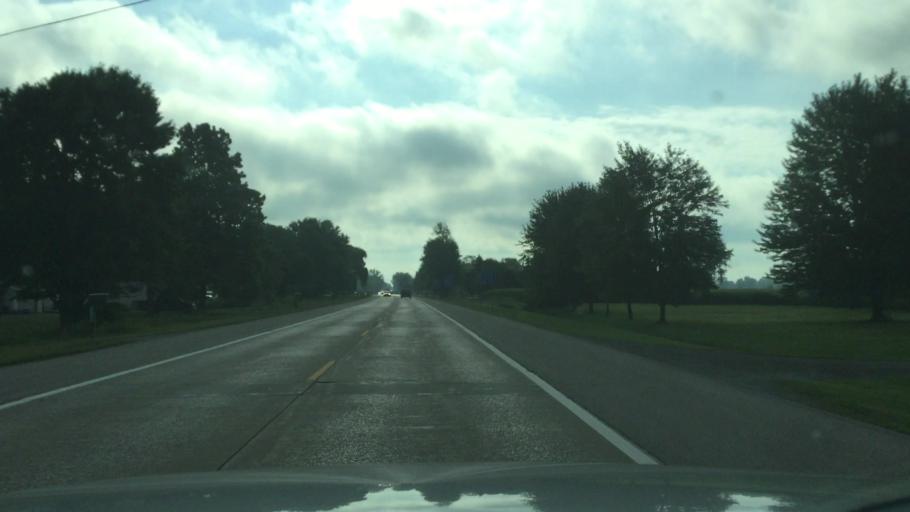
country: US
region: Michigan
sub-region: Saginaw County
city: Birch Run
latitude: 43.2499
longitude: -83.7452
